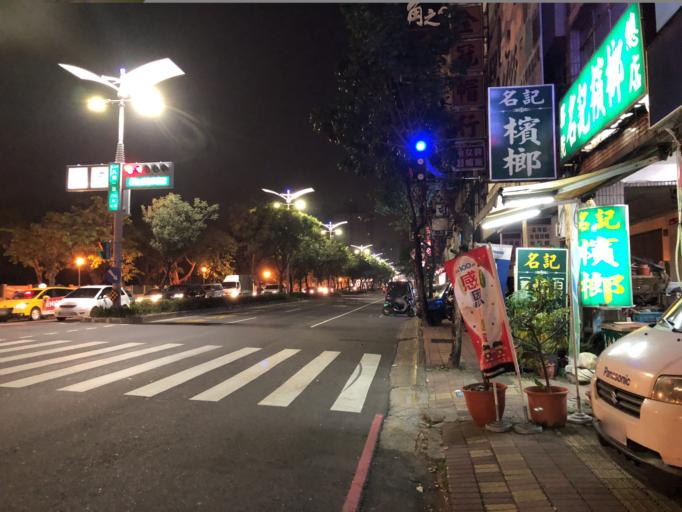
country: TW
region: Kaohsiung
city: Kaohsiung
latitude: 22.6383
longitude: 120.3322
